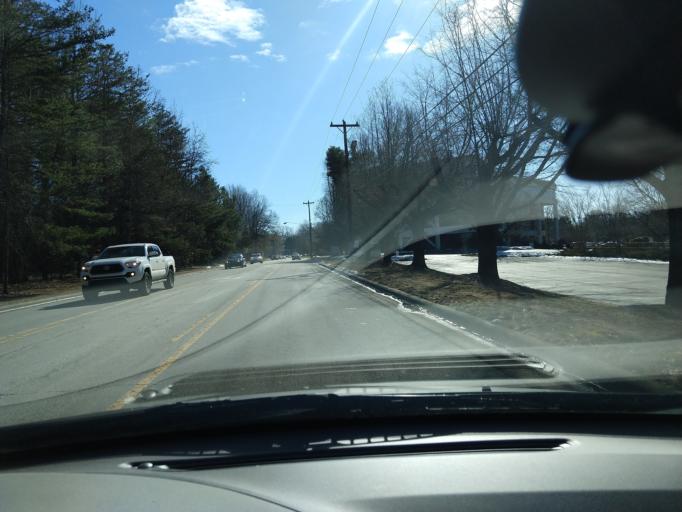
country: US
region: North Carolina
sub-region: Guilford County
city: Greensboro
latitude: 36.1227
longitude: -79.8430
